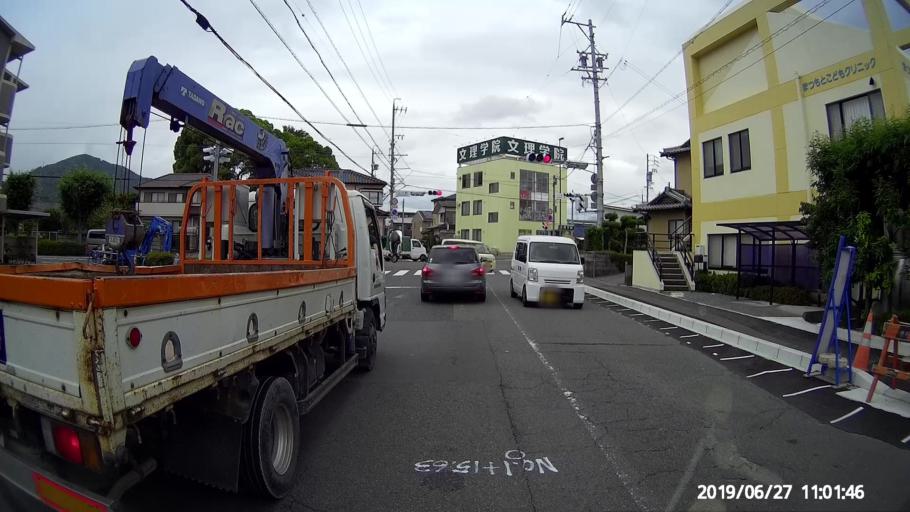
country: JP
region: Shizuoka
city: Shizuoka-shi
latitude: 34.9448
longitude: 138.3662
